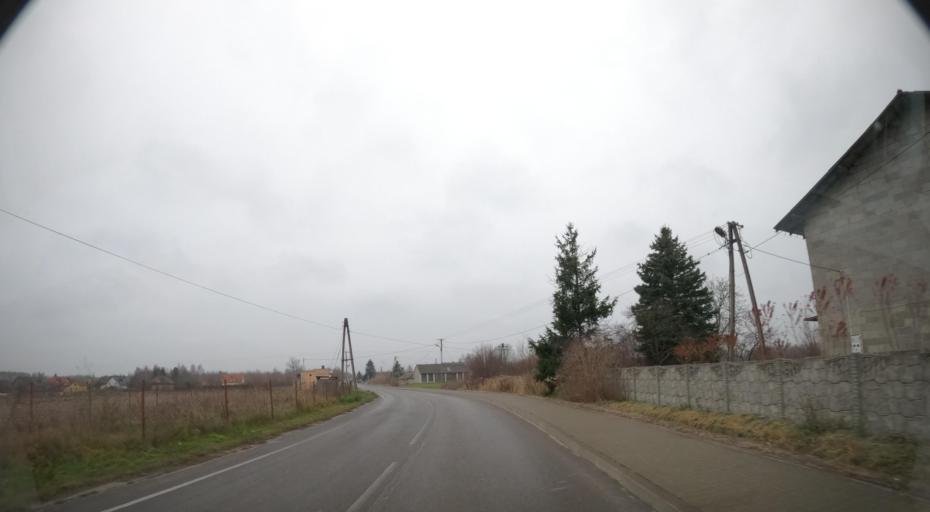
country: PL
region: Masovian Voivodeship
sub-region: Powiat radomski
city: Skaryszew
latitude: 51.3844
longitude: 21.2554
